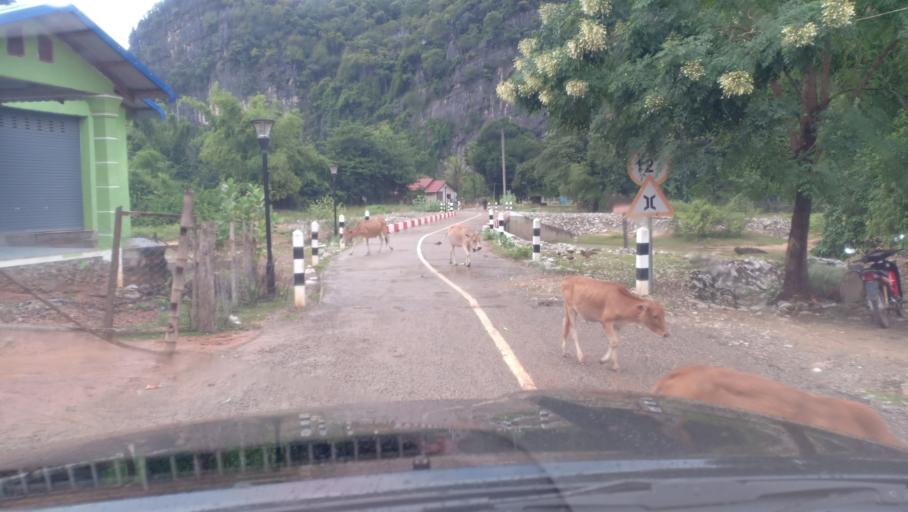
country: LA
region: Khammouan
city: Thakhek
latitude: 17.4286
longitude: 104.8635
